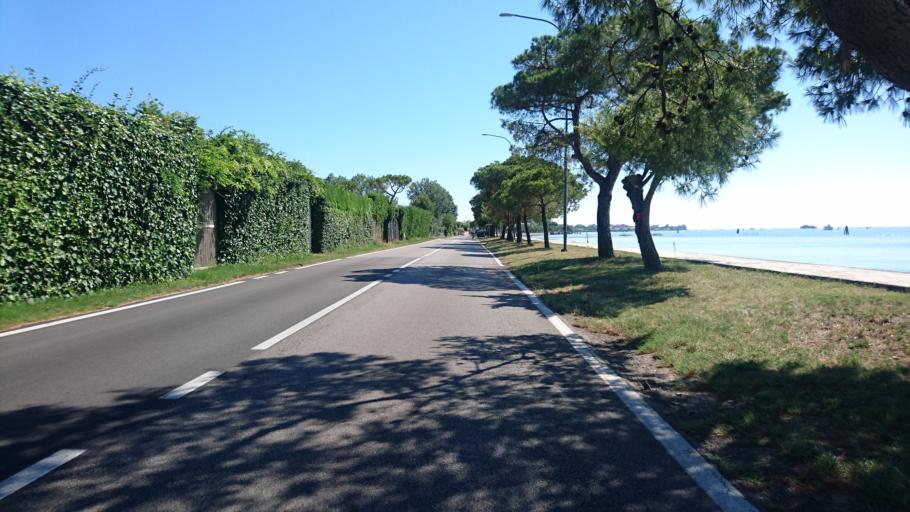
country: IT
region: Veneto
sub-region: Provincia di Venezia
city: San Pietro in Volta
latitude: 45.3627
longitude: 12.3331
